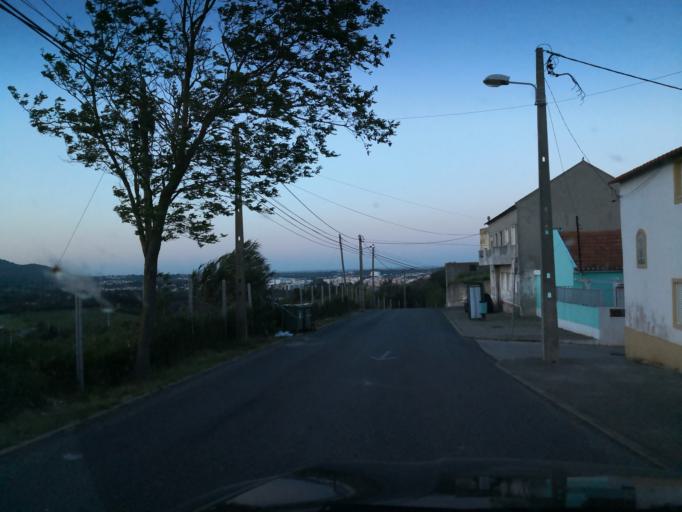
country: PT
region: Setubal
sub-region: Setubal
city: Setubal
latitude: 38.5281
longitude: -8.9109
